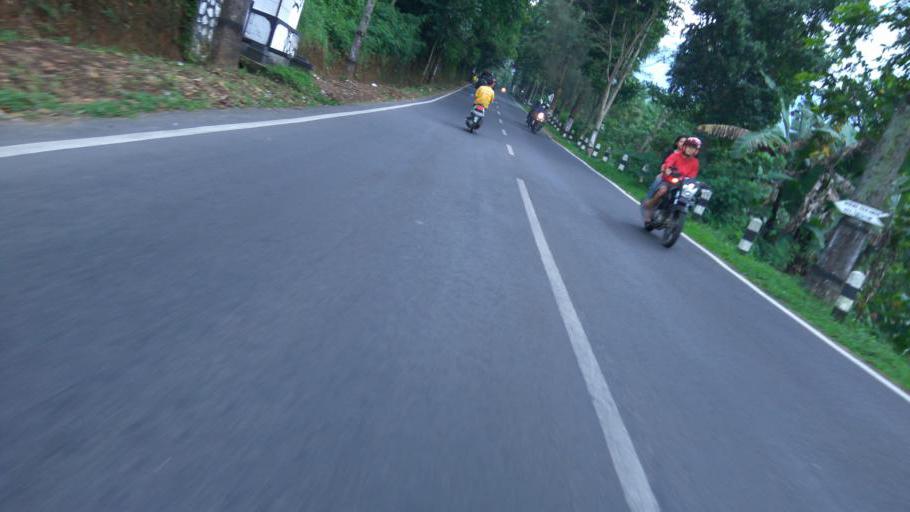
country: ID
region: Central Java
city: Gunung Kendil
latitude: -7.3761
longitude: 110.4273
